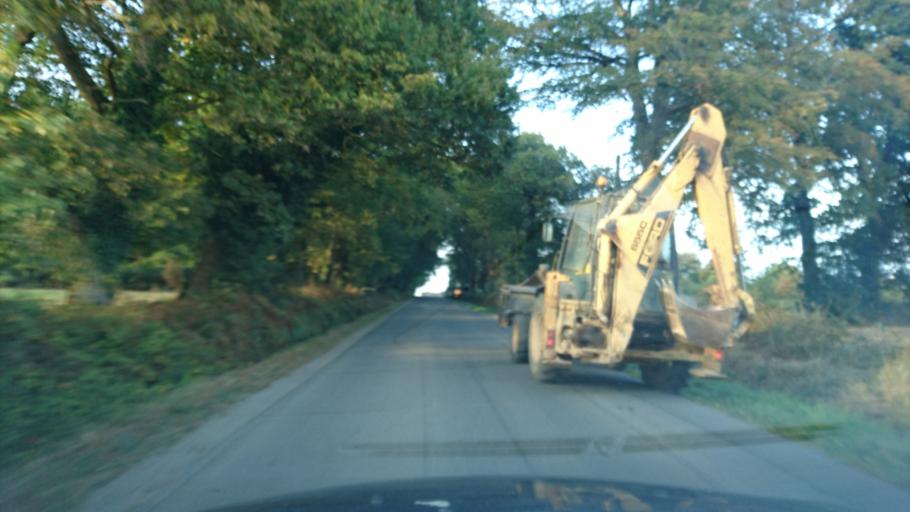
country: FR
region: Brittany
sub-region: Departement d'Ille-et-Vilaine
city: Bains-sur-Oust
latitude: 47.7331
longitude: -2.0502
